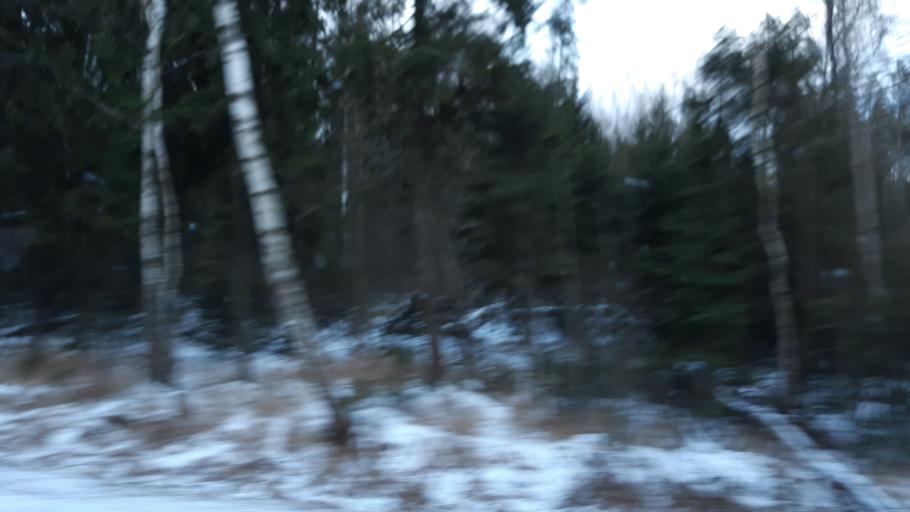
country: RU
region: Moskovskaya
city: Noginsk-9
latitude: 55.9625
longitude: 38.5422
